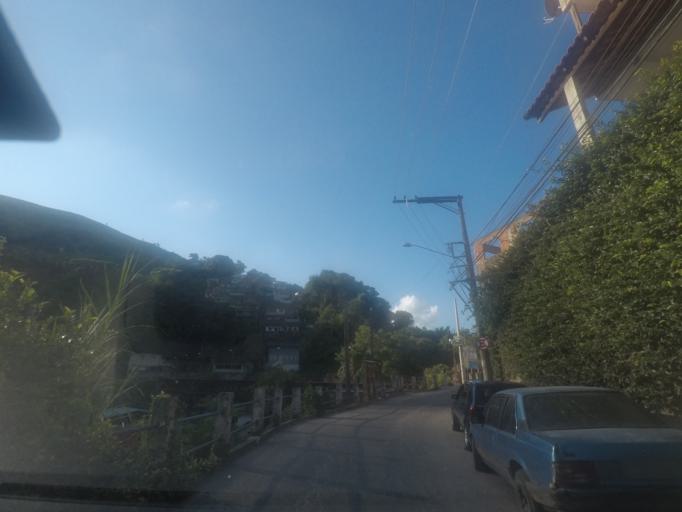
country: BR
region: Rio de Janeiro
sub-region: Petropolis
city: Petropolis
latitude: -22.4964
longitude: -43.1496
